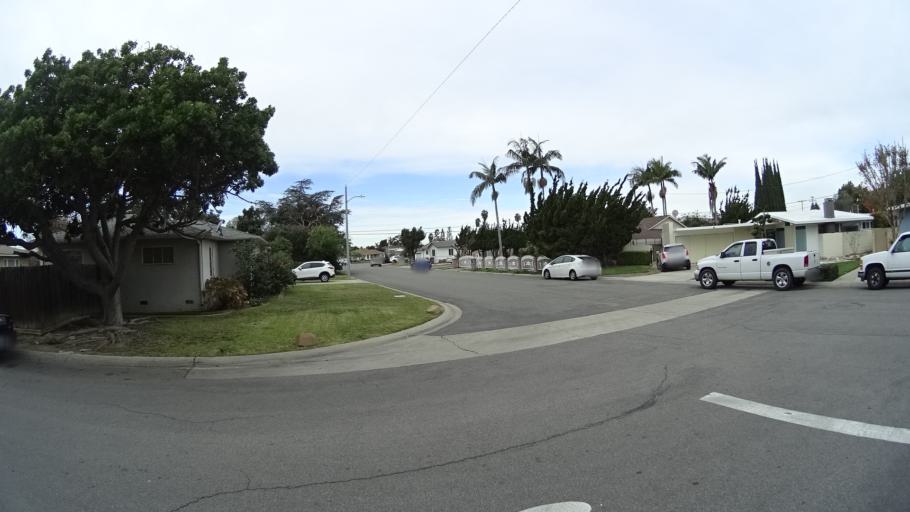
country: US
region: California
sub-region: Orange County
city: Garden Grove
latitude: 33.7712
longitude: -117.9348
